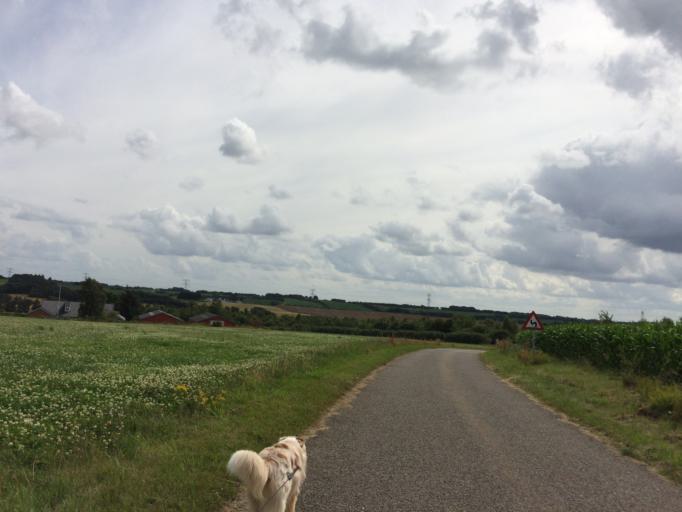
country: DK
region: Central Jutland
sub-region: Viborg Kommune
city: Viborg
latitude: 56.4963
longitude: 9.5312
